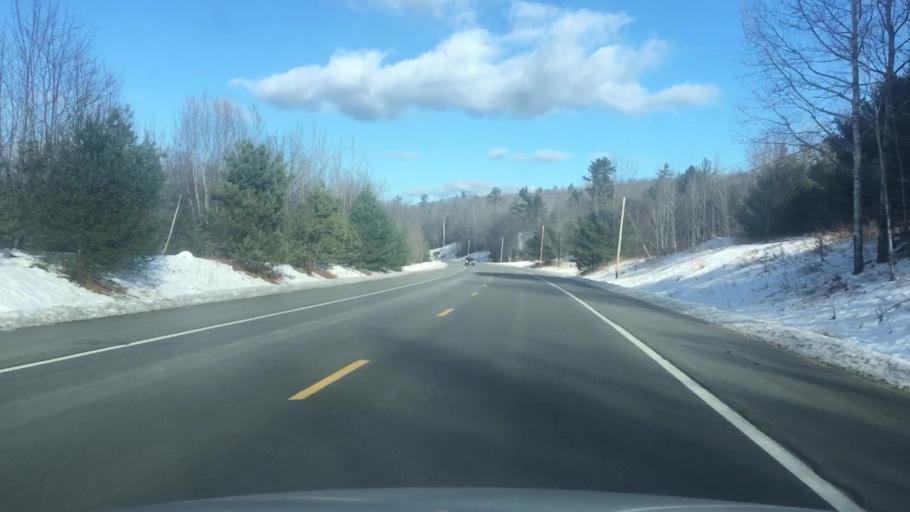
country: US
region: Maine
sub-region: Somerset County
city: Madison
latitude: 44.9991
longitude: -69.8591
